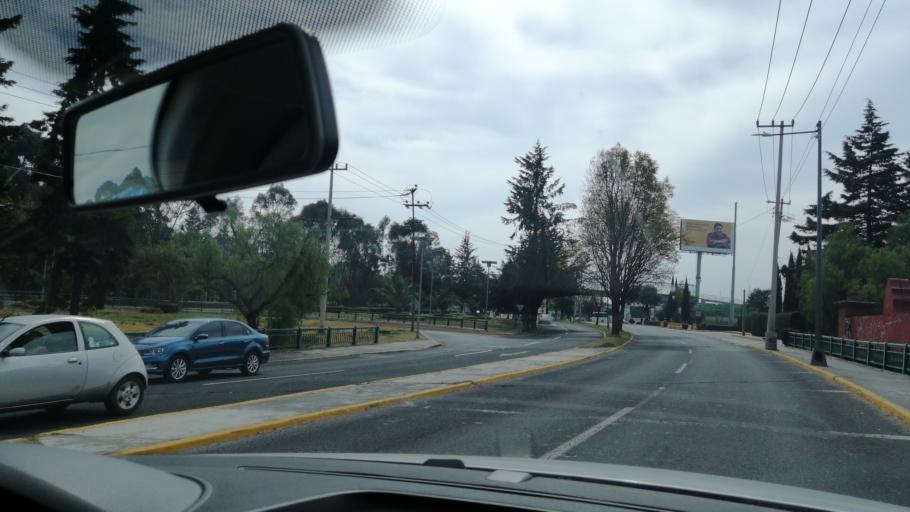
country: MX
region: Mexico
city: San Buenaventura
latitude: 19.2880
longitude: -99.6803
